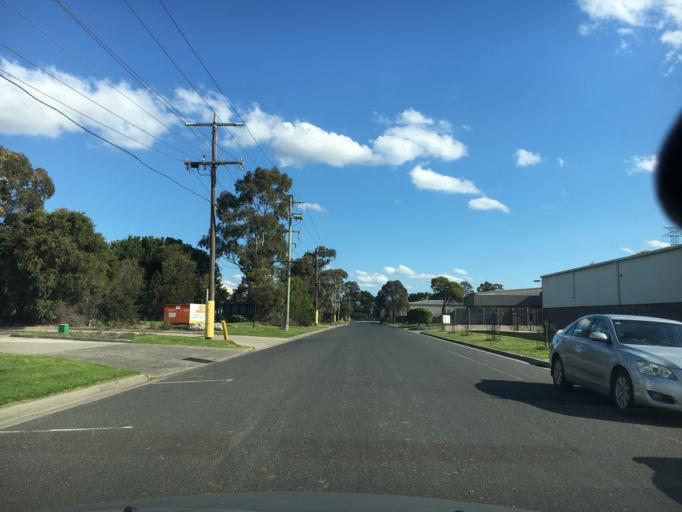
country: AU
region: Victoria
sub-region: Greater Dandenong
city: Springvale
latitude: -37.9299
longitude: 145.1479
